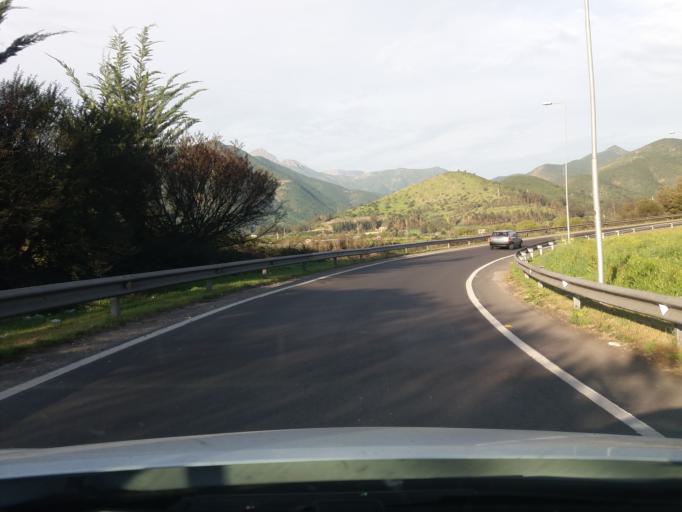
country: CL
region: Valparaiso
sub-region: Provincia de Quillota
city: Hacienda La Calera
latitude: -32.7864
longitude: -71.1686
